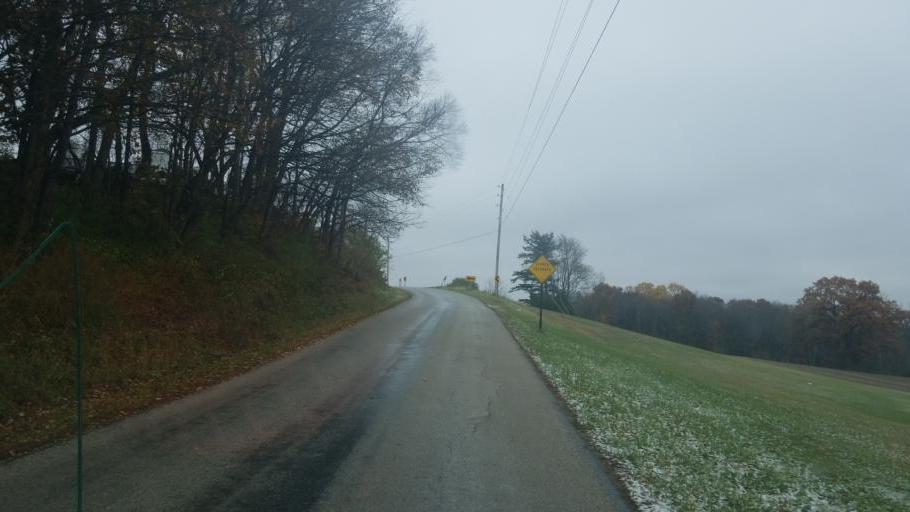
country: US
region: Ohio
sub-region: Richland County
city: Lincoln Heights
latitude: 40.8242
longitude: -82.4433
